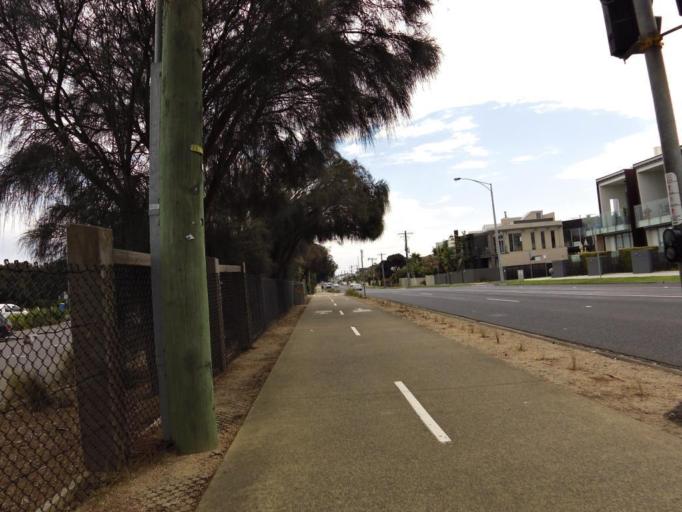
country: AU
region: Victoria
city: Hampton
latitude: -37.9582
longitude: 145.0090
